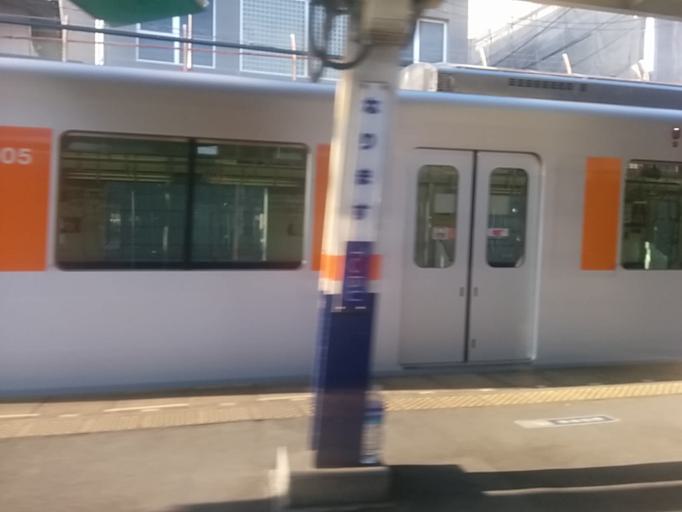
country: JP
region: Saitama
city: Wako
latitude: 35.7769
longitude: 139.6338
